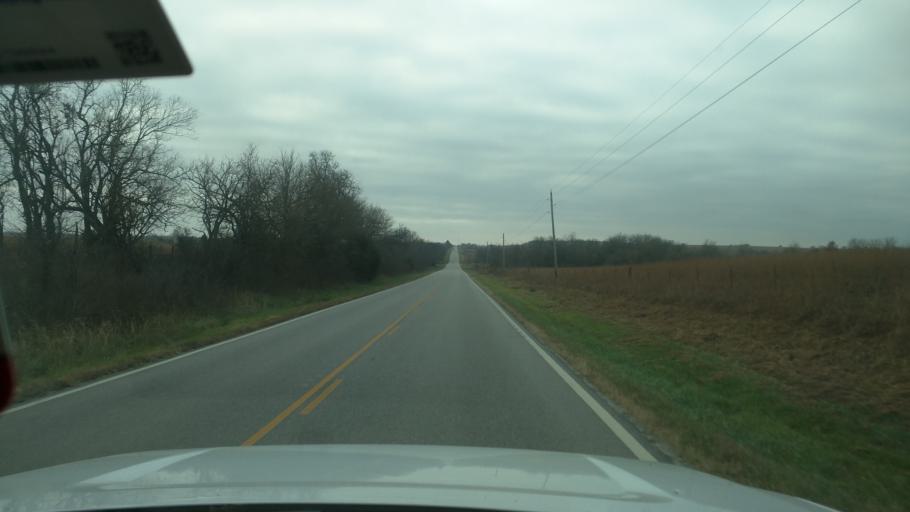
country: US
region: Kansas
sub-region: Greenwood County
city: Eureka
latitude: 37.6829
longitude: -96.2344
